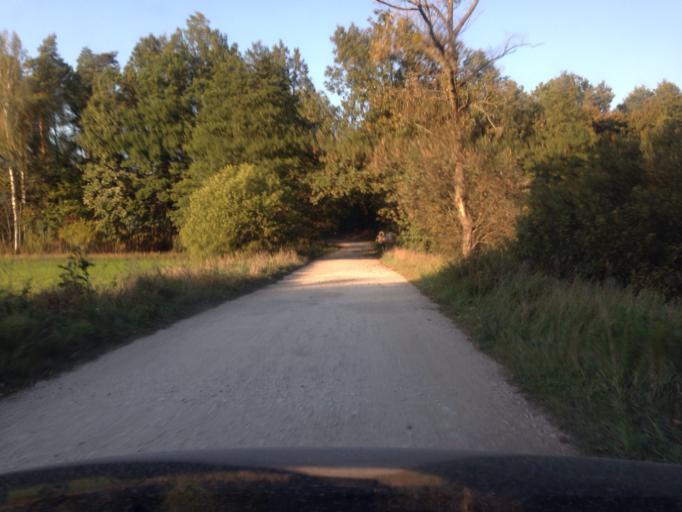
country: PL
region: Kujawsko-Pomorskie
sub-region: Powiat brodnicki
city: Gorzno
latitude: 53.2362
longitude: 19.6588
